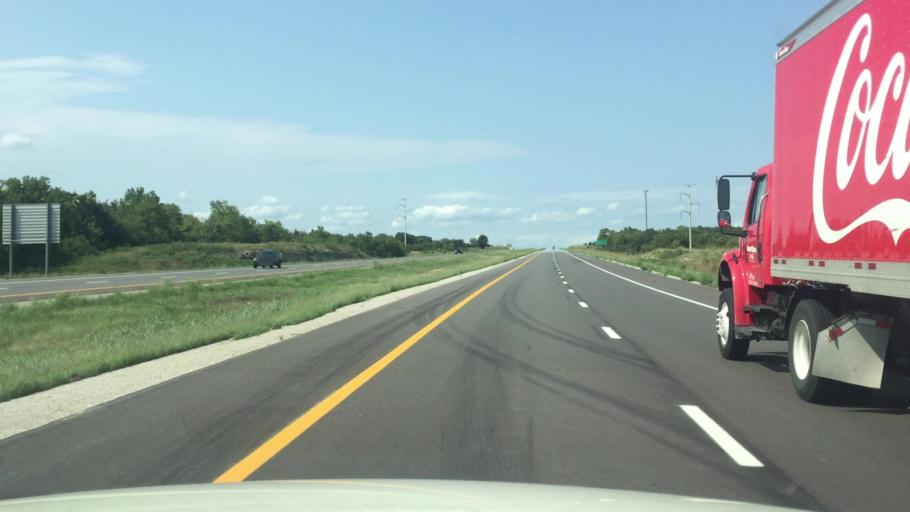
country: US
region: Kansas
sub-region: Linn County
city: La Cygne
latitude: 38.3574
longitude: -94.6874
